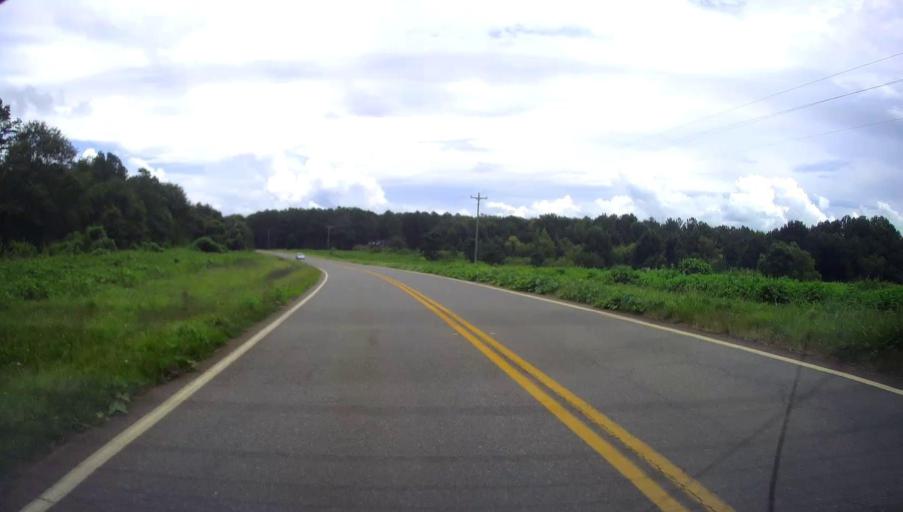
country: US
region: Georgia
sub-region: Schley County
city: Ellaville
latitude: 32.2527
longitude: -84.4001
